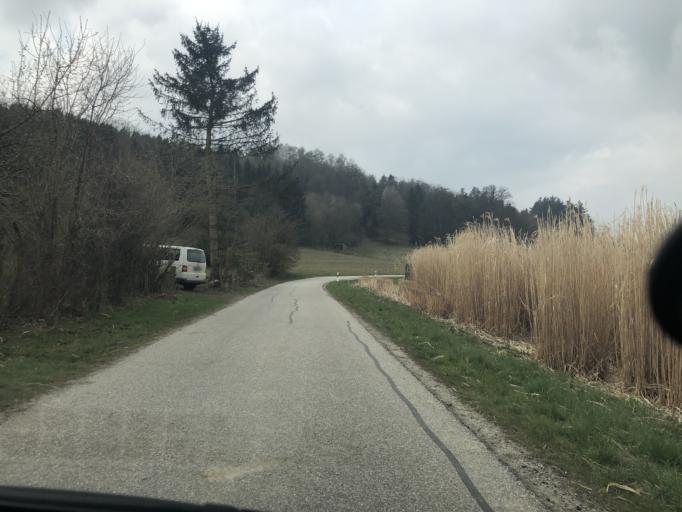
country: DE
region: Bavaria
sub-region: Upper Bavaria
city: Wolfersdorf
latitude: 48.4422
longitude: 11.7119
